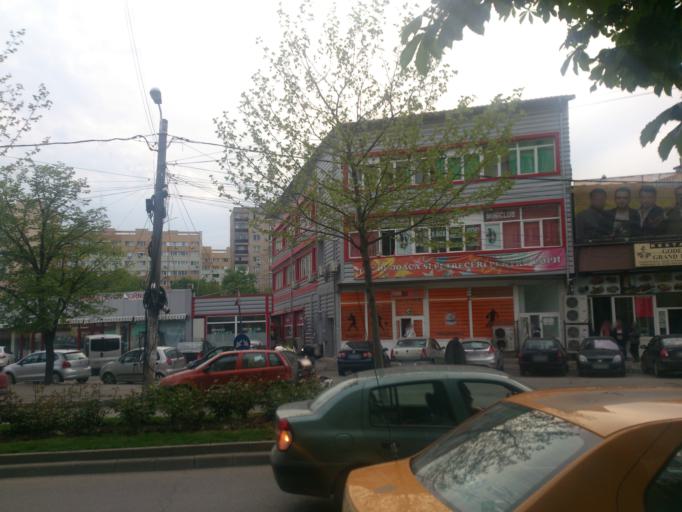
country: RO
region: Ilfov
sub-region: Comuna Chiajna
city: Rosu
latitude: 44.4347
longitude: 26.0207
